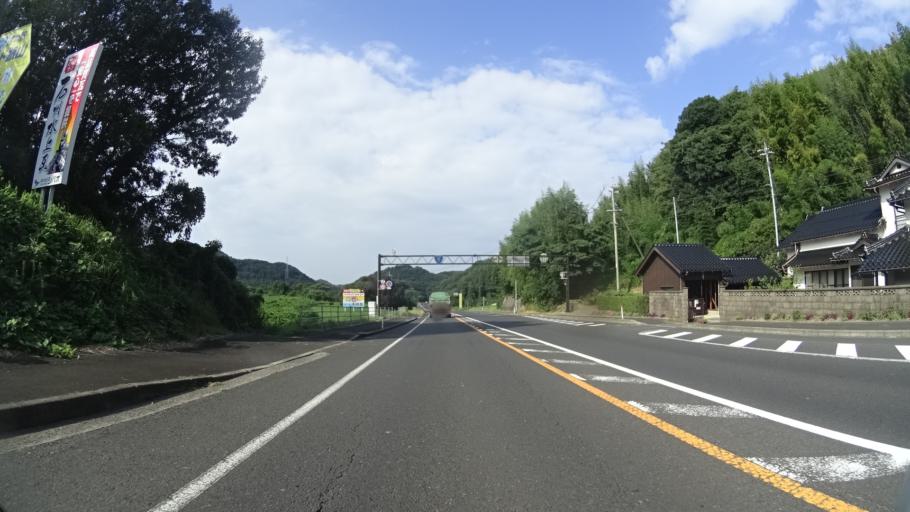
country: JP
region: Shimane
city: Odacho-oda
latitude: 35.2458
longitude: 132.5535
